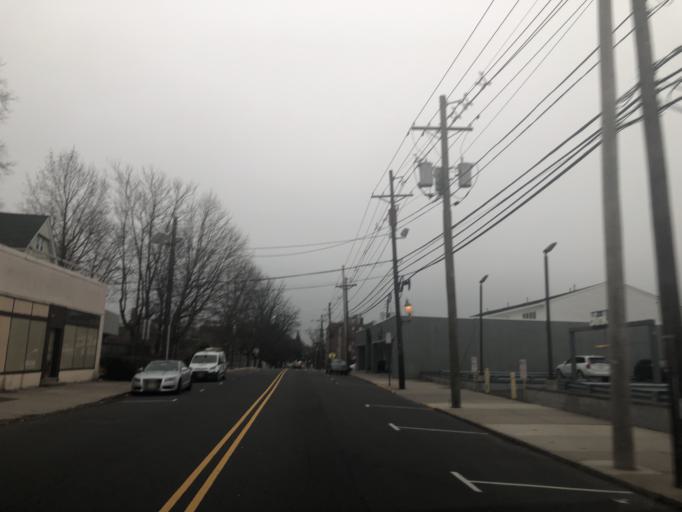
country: US
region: New Jersey
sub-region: Essex County
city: Maplewood
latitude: 40.7385
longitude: -74.2652
